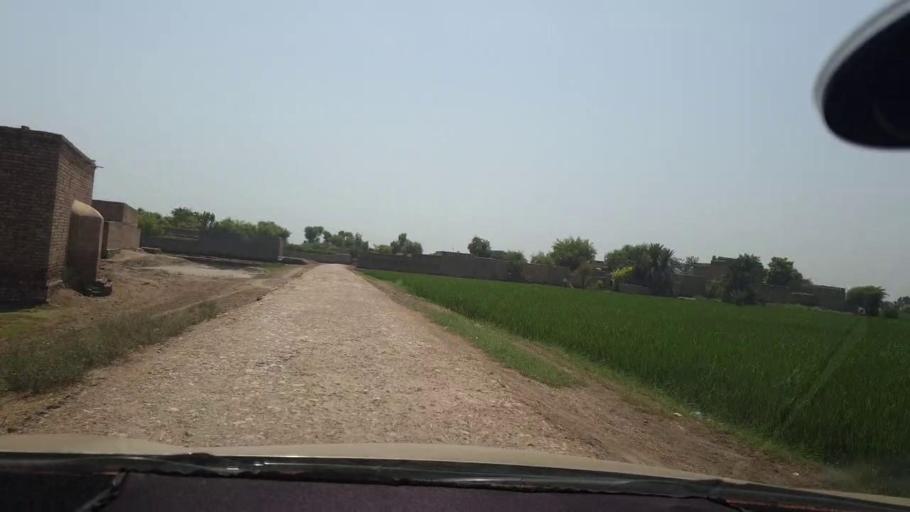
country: PK
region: Sindh
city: Kambar
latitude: 27.6358
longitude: 67.9333
